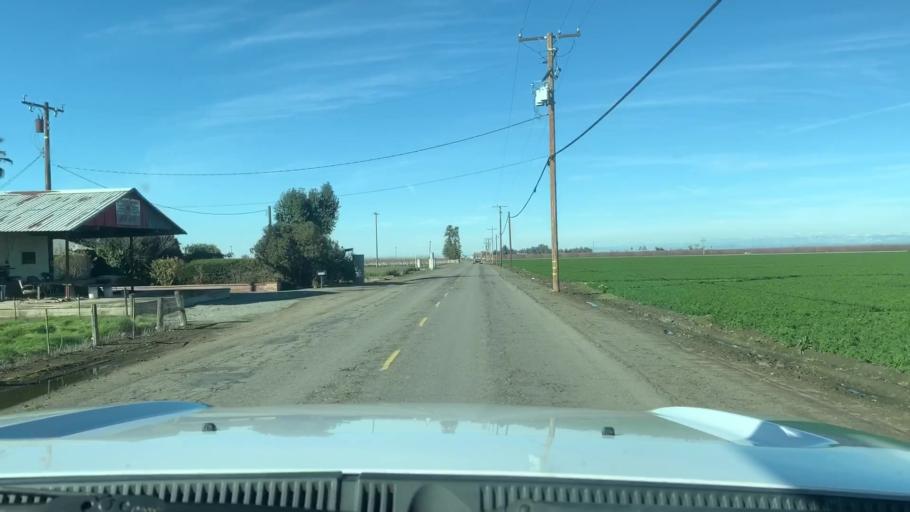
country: US
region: California
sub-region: Kings County
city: Corcoran
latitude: 36.2058
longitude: -119.4930
